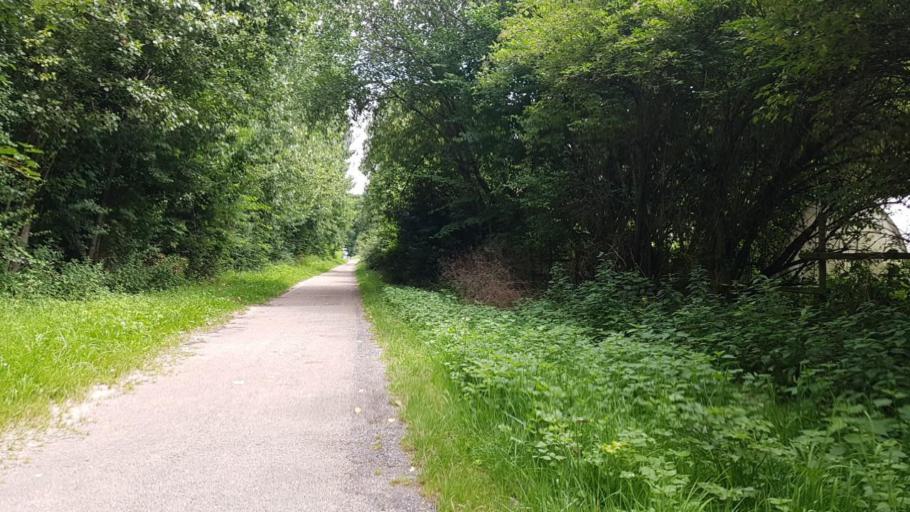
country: FR
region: Picardie
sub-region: Departement de l'Aisne
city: Esqueheries
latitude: 49.8994
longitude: 3.7386
